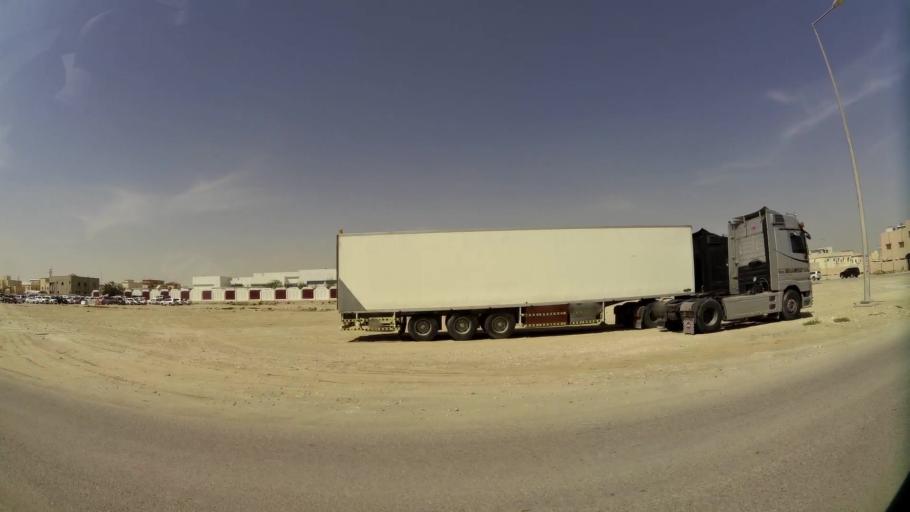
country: QA
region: Baladiyat ar Rayyan
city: Ar Rayyan
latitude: 25.2482
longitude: 51.3952
